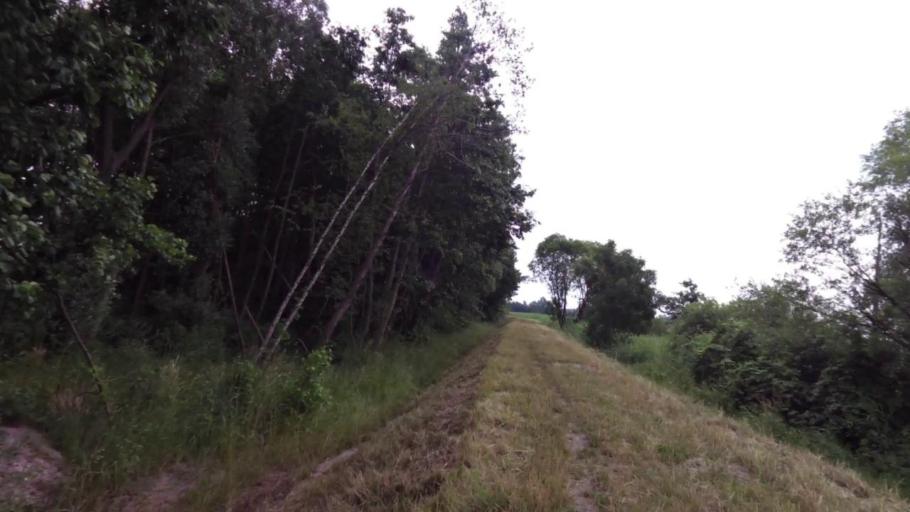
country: PL
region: West Pomeranian Voivodeship
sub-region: Szczecin
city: Szczecin
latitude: 53.4159
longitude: 14.6577
